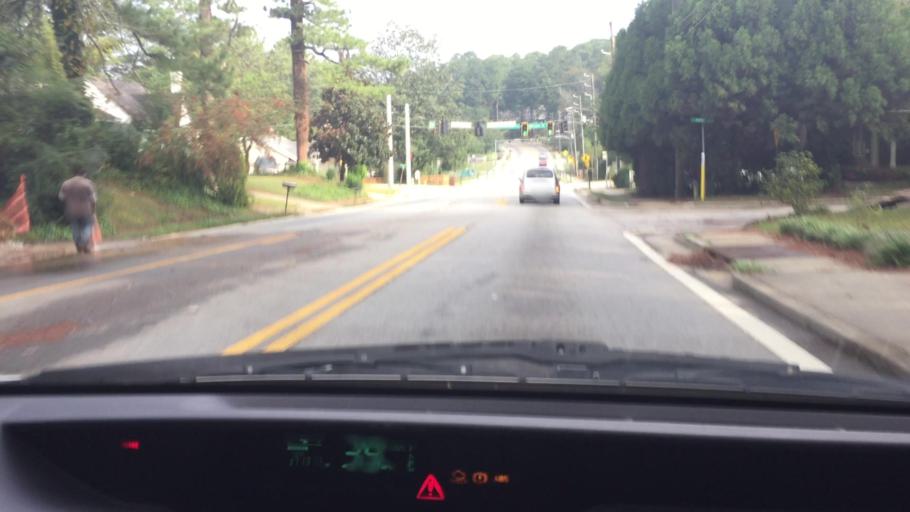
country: US
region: Georgia
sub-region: DeKalb County
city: Decatur
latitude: 33.7556
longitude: -84.2915
